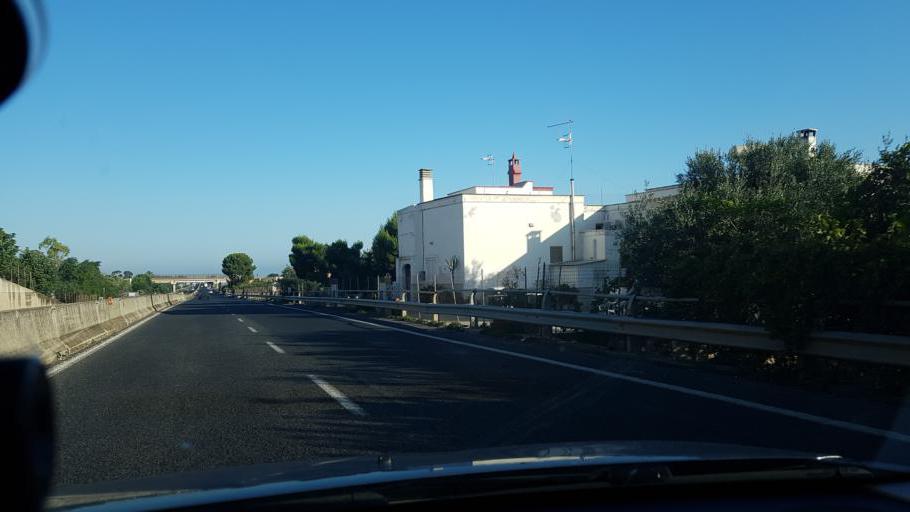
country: IT
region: Apulia
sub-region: Provincia di Brindisi
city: Fasano
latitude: 40.8905
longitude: 17.3330
